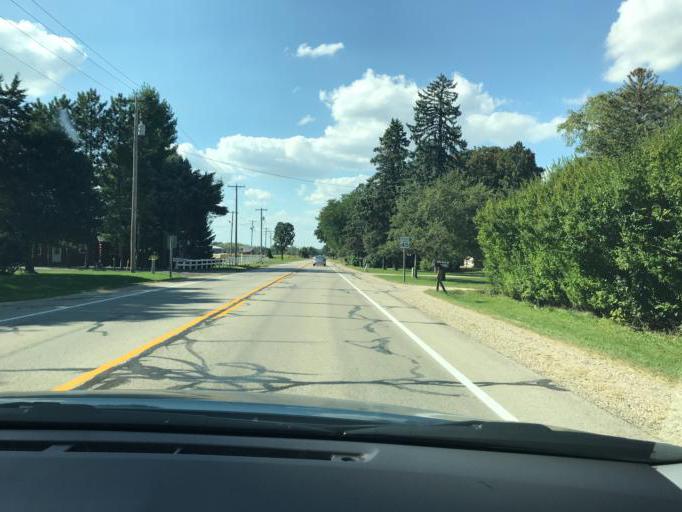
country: US
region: Wisconsin
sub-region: Walworth County
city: Williams Bay
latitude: 42.6127
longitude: -88.5687
